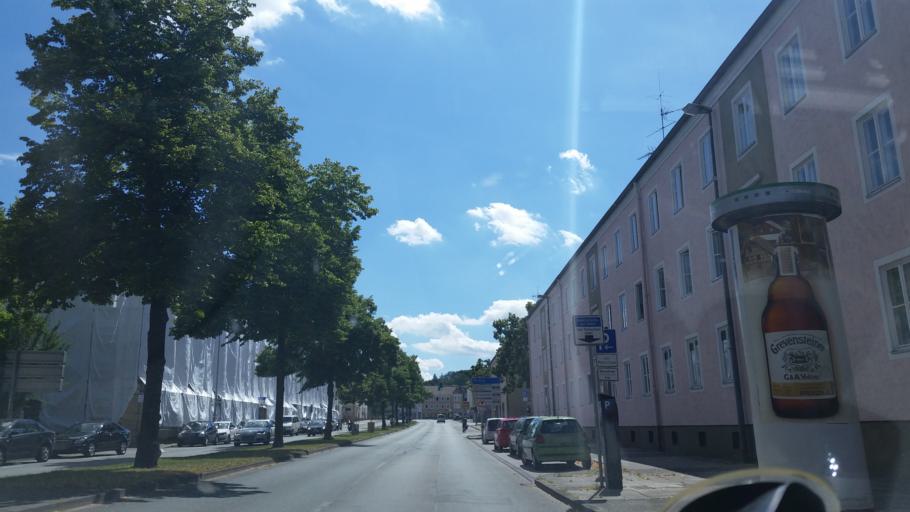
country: DE
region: Lower Saxony
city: Wolfsburg
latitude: 52.4210
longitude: 10.7843
